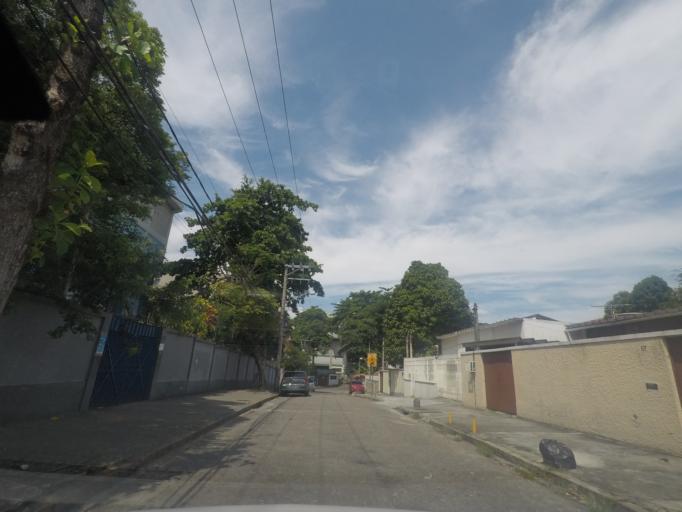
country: BR
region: Rio de Janeiro
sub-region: Rio De Janeiro
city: Rio de Janeiro
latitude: -22.8127
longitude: -43.2096
